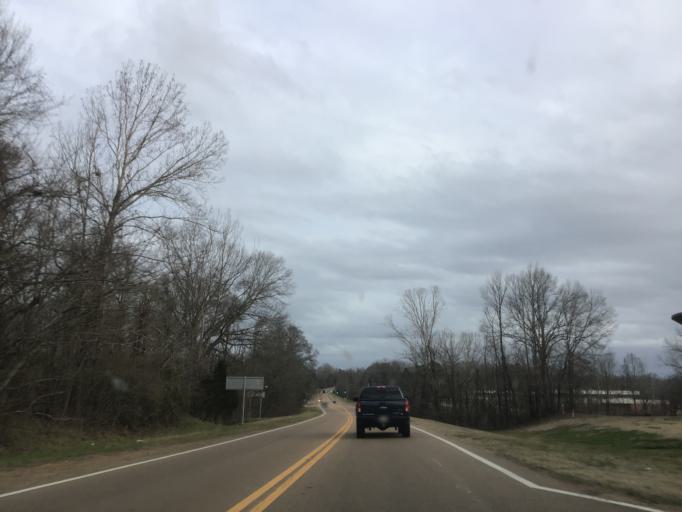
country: US
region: Mississippi
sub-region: Warren County
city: Beechwood
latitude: 32.3345
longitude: -90.8237
